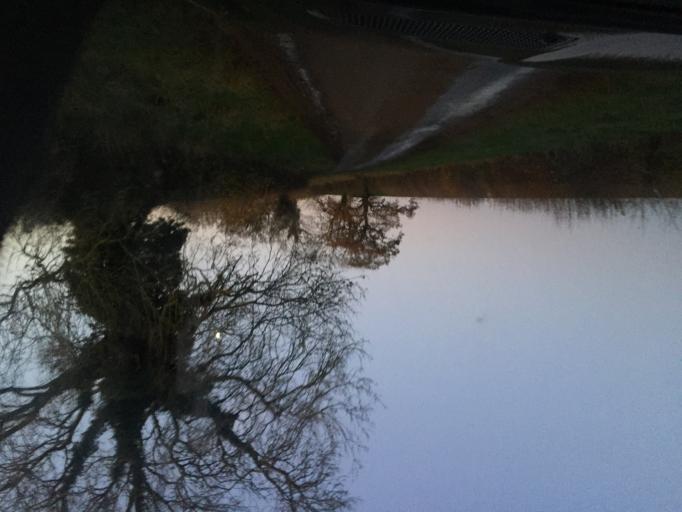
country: GB
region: England
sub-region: Northamptonshire
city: Brackley
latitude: 52.0919
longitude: -1.1061
